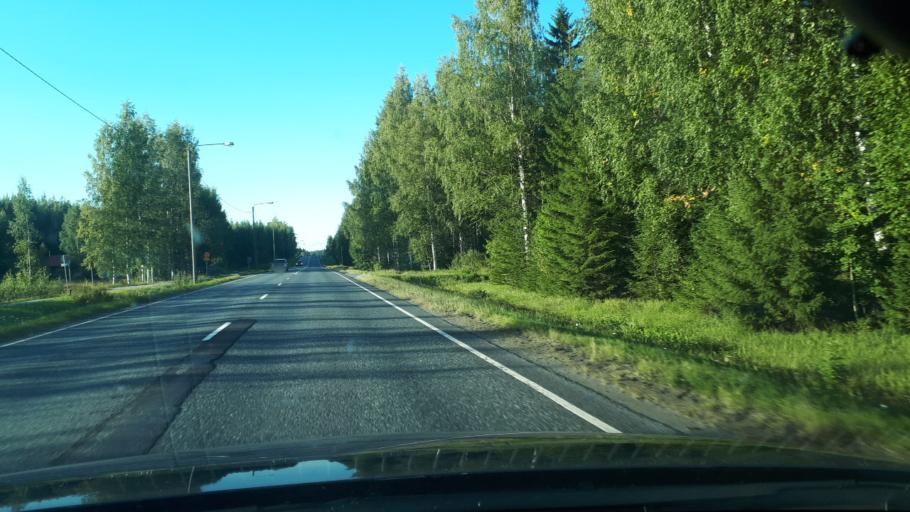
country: FI
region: Northern Savo
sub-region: Ylae-Savo
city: Lapinlahti
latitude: 63.4278
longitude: 27.3288
